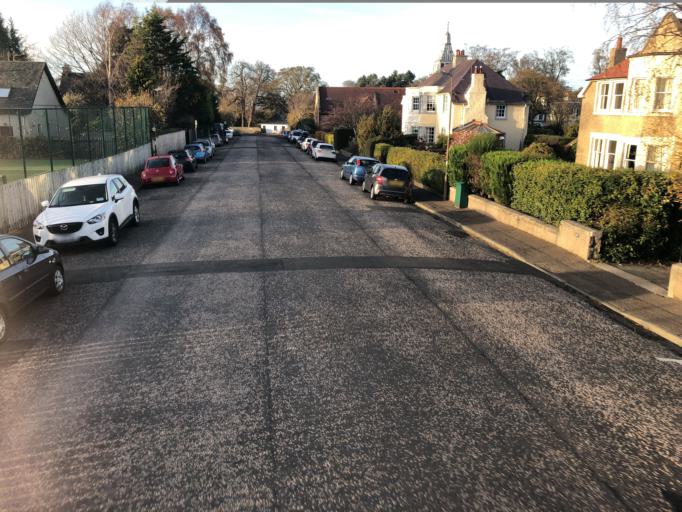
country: GB
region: Scotland
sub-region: Edinburgh
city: Colinton
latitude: 55.9067
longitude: -3.2530
